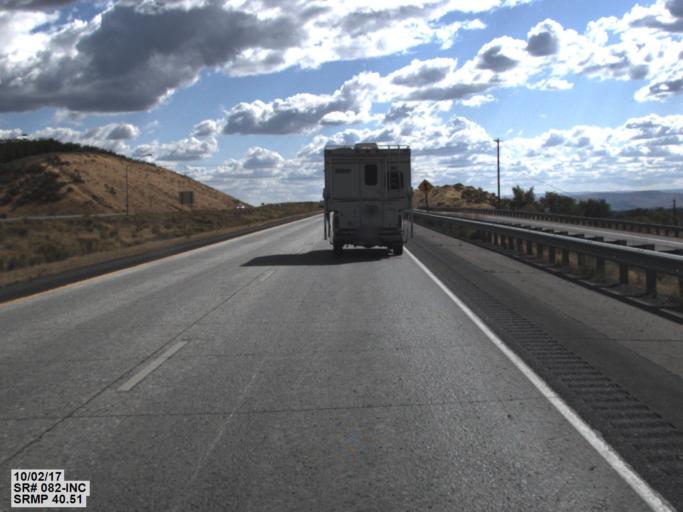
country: US
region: Washington
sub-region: Yakima County
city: Union Gap
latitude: 46.5089
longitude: -120.4516
